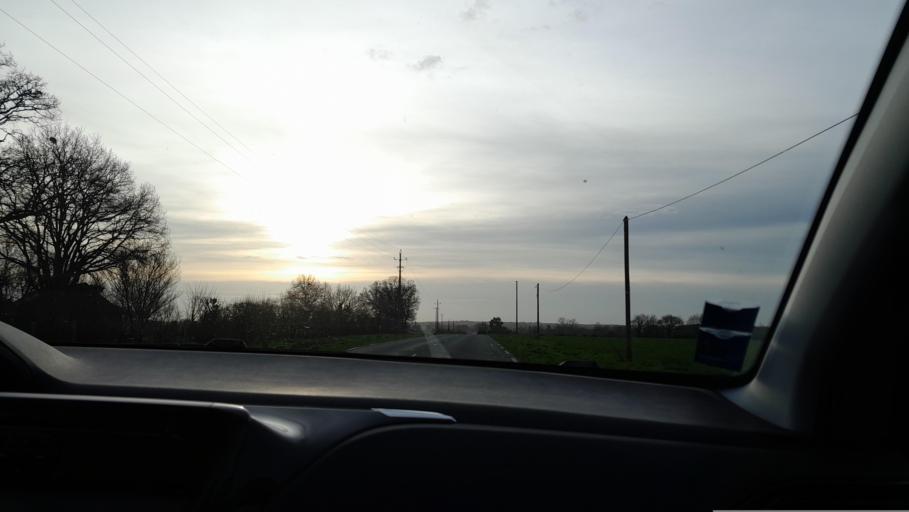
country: FR
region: Pays de la Loire
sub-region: Departement de la Mayenne
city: Ballots
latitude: 47.9269
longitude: -1.0729
